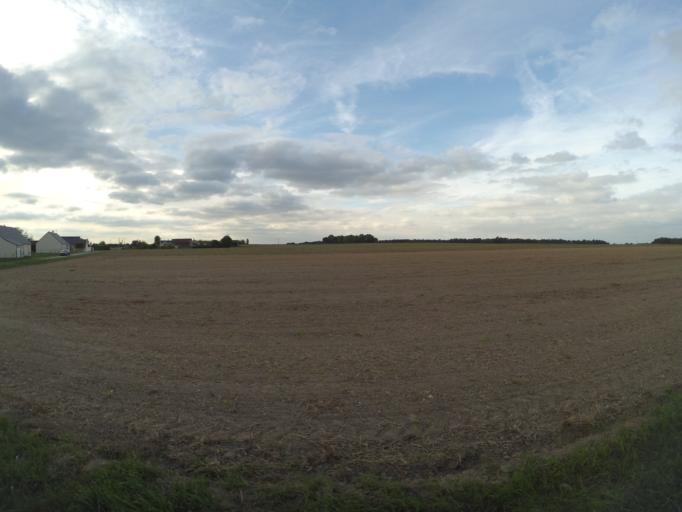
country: FR
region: Centre
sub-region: Departement d'Indre-et-Loire
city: Nazelles-Negron
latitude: 47.4482
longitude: 0.9683
